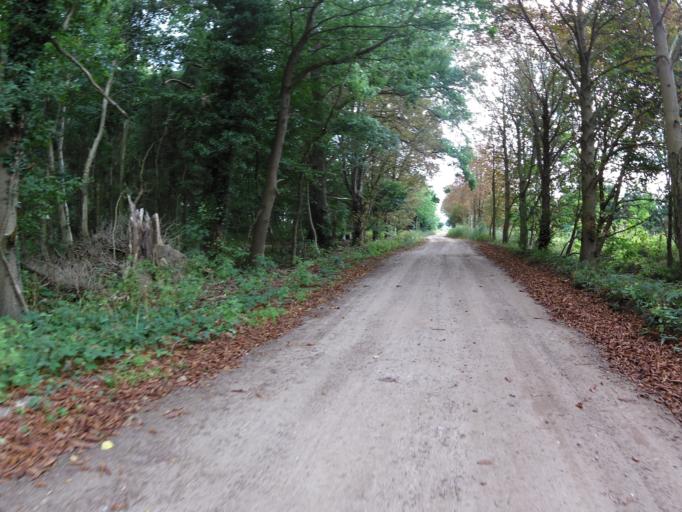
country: DE
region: Mecklenburg-Vorpommern
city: Loddin
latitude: 53.9979
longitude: 14.0605
